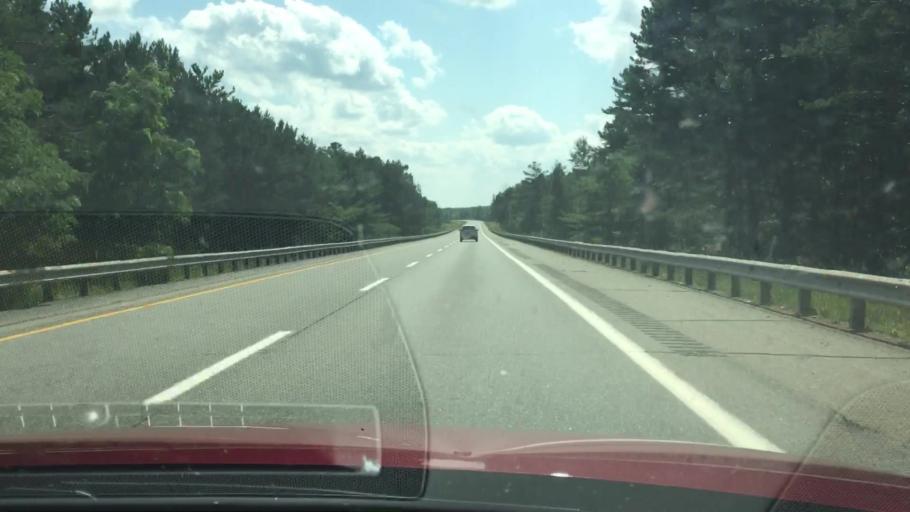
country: US
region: Maine
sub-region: Penobscot County
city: Lincoln
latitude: 45.3931
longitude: -68.6024
